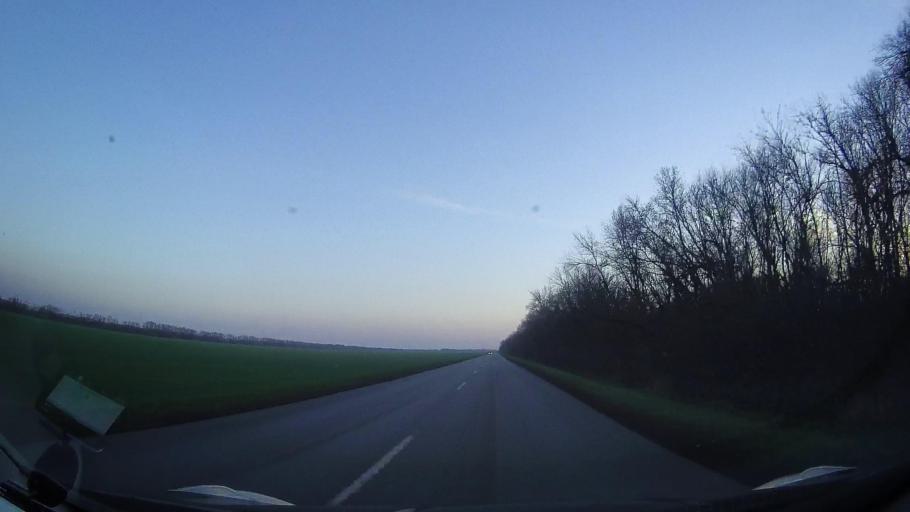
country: RU
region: Rostov
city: Zernograd
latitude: 46.9880
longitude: 40.3915
